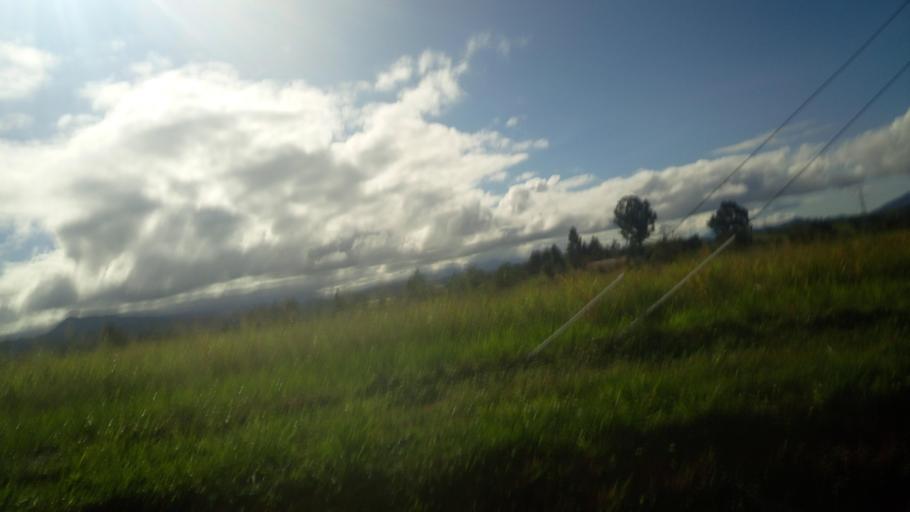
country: AU
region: Queensland
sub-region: Cassowary Coast
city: Innisfail
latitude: -17.5342
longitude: 145.9730
